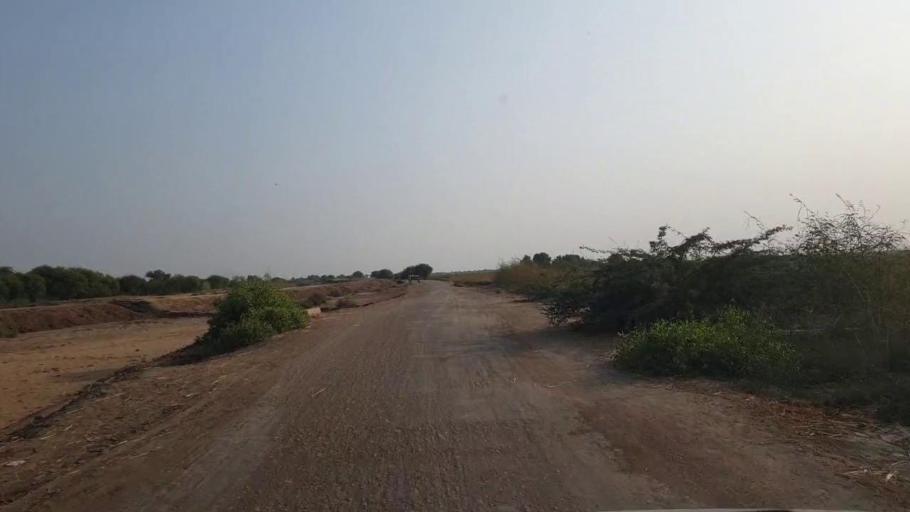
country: PK
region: Sindh
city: Matli
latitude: 25.0543
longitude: 68.7633
